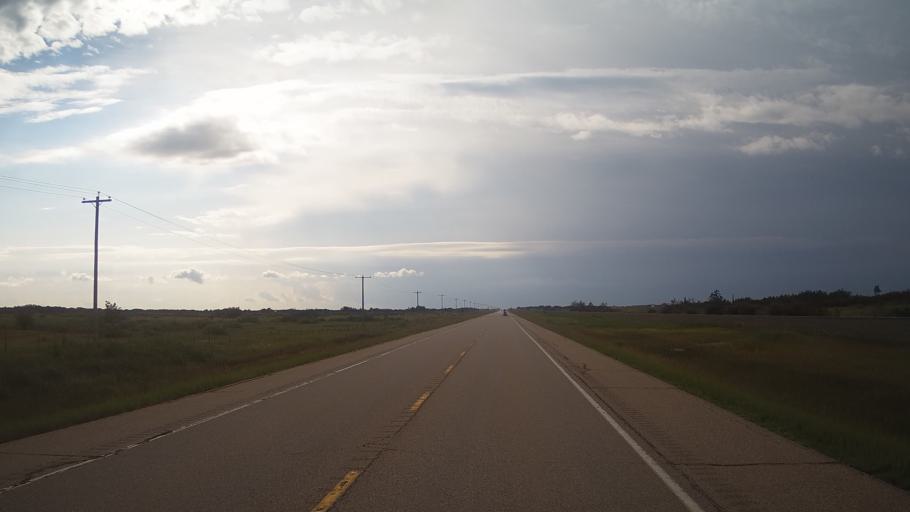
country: CA
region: Alberta
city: Viking
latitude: 53.1407
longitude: -111.9380
